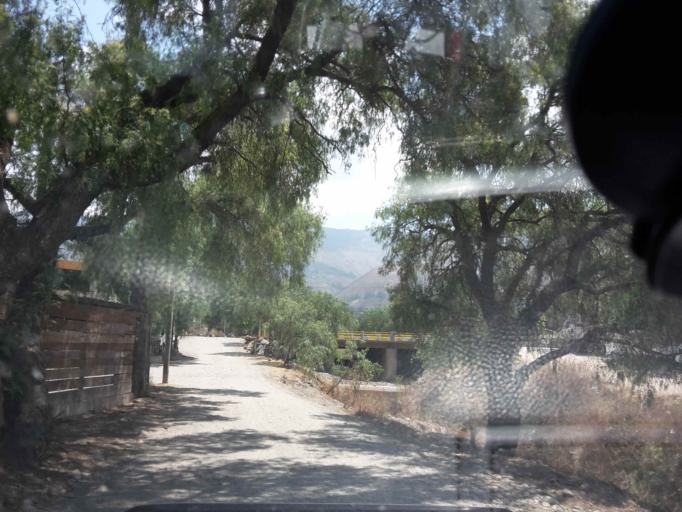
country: BO
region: Cochabamba
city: Cochabamba
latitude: -17.3426
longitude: -66.2125
